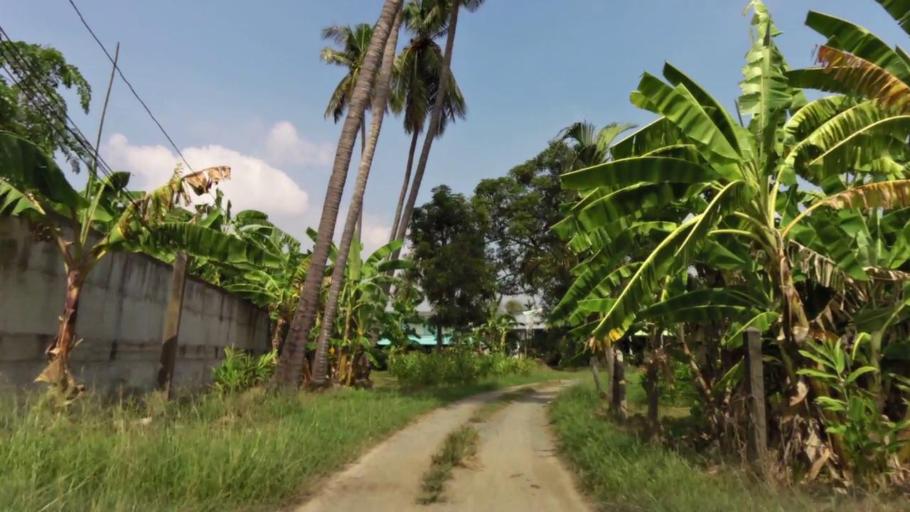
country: TH
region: Ang Thong
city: Ang Thong
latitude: 14.6070
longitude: 100.4030
